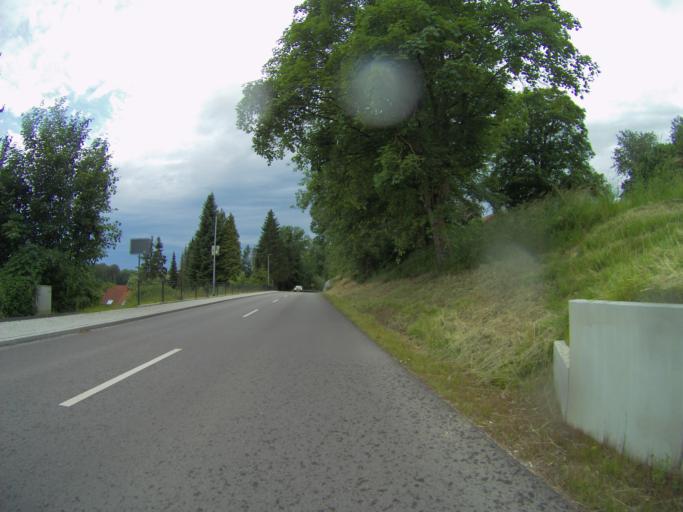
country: DE
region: Bavaria
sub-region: Upper Bavaria
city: Marzling
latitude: 48.4102
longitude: 11.7903
